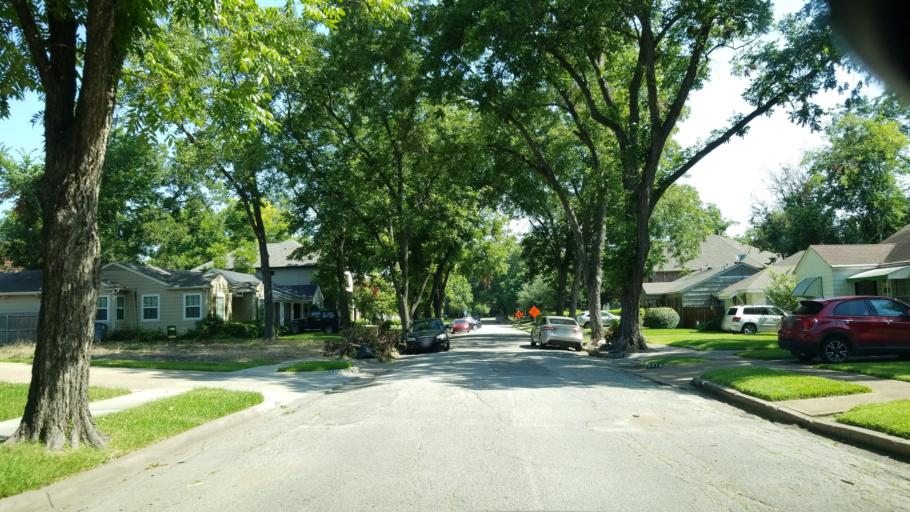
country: US
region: Texas
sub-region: Dallas County
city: Highland Park
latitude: 32.8388
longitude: -96.7645
